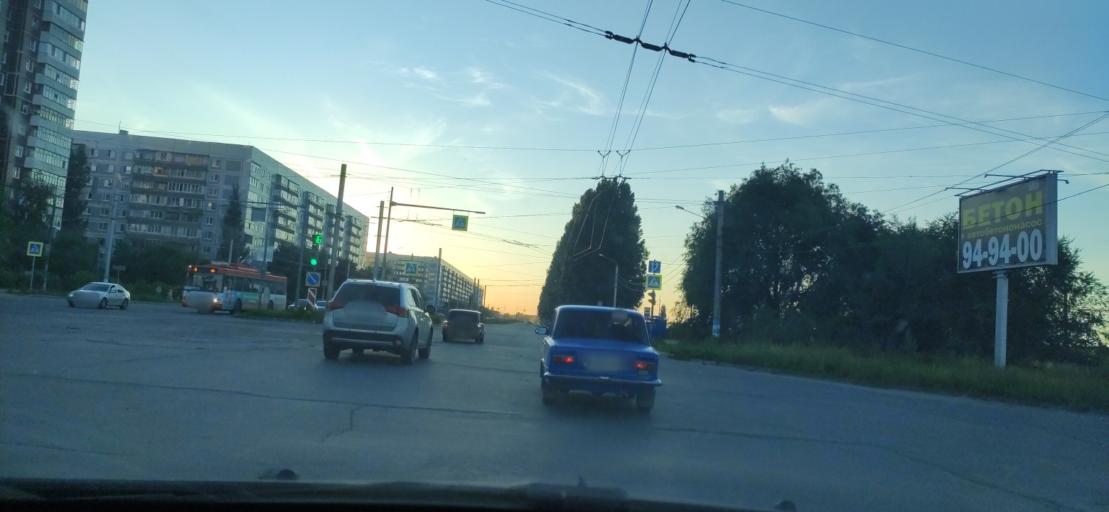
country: RU
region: Ulyanovsk
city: Mirnyy
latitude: 54.3820
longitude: 48.6208
